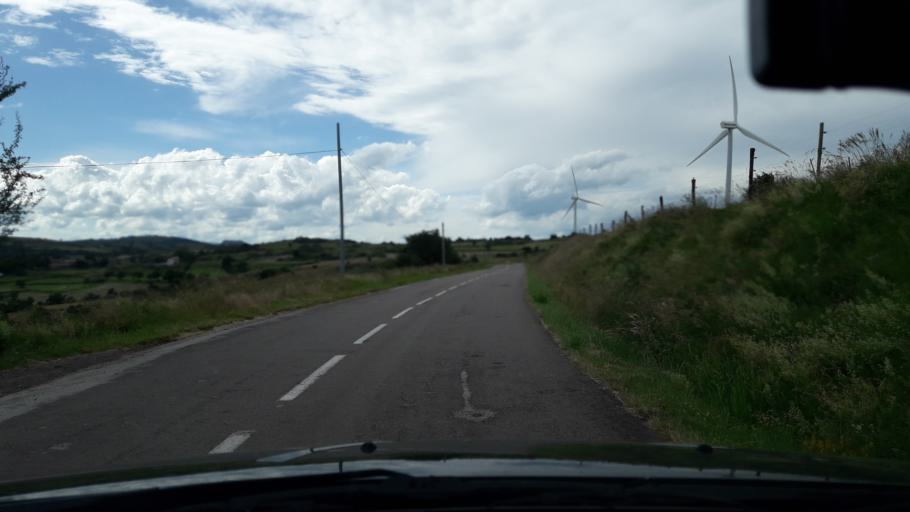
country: FR
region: Rhone-Alpes
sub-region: Departement de l'Ardeche
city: Saint-Priest
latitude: 44.6743
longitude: 4.5576
